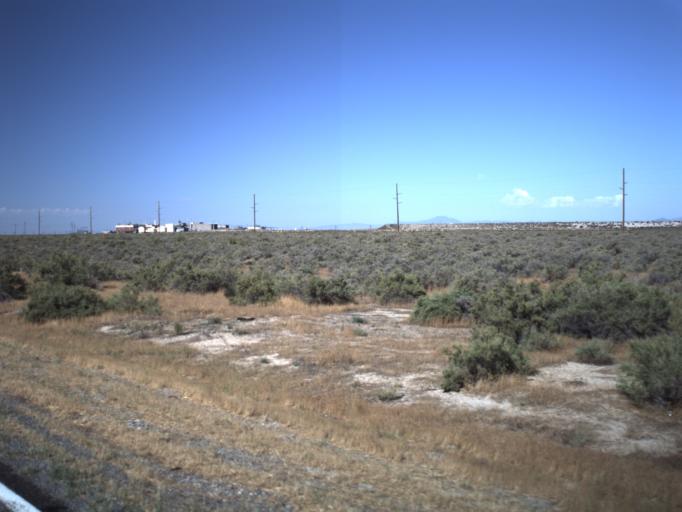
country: US
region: Utah
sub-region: Millard County
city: Delta
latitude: 39.4733
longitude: -112.4211
